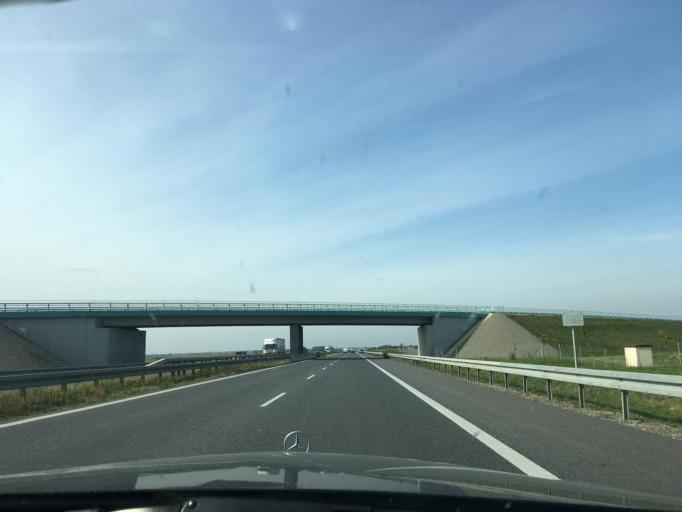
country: PL
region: Lower Silesian Voivodeship
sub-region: Powiat olesnicki
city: Olesnica
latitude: 51.2256
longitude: 17.3498
